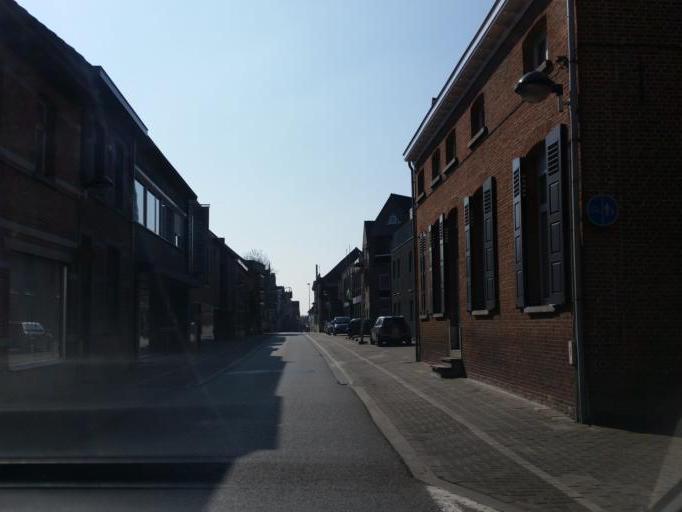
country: BE
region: Flanders
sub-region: Provincie Oost-Vlaanderen
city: Kruibeke
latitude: 51.1729
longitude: 4.3139
